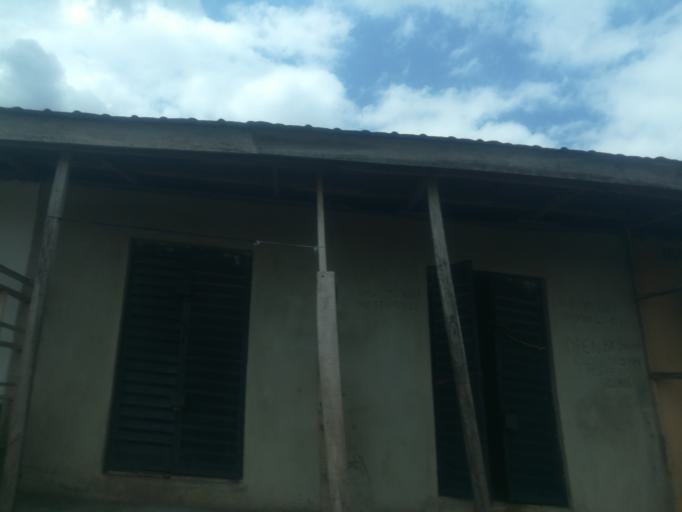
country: NG
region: Oyo
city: Egbeda
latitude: 7.4169
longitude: 4.0025
